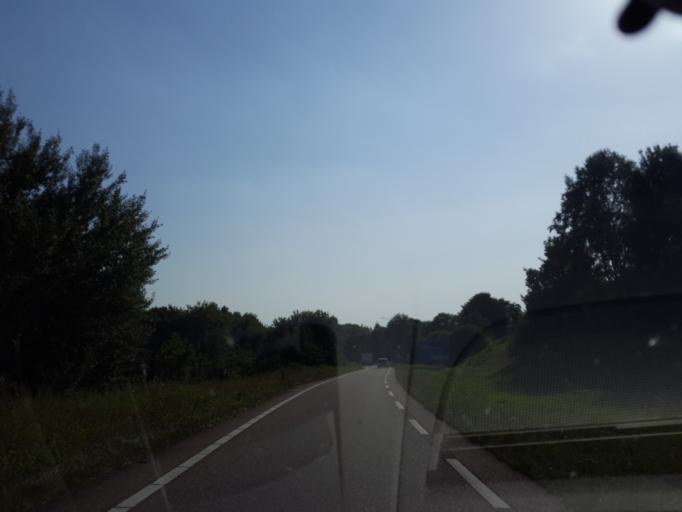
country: NL
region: North Brabant
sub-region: Gemeente Helmond
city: Helmond
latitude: 51.4738
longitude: 5.7154
